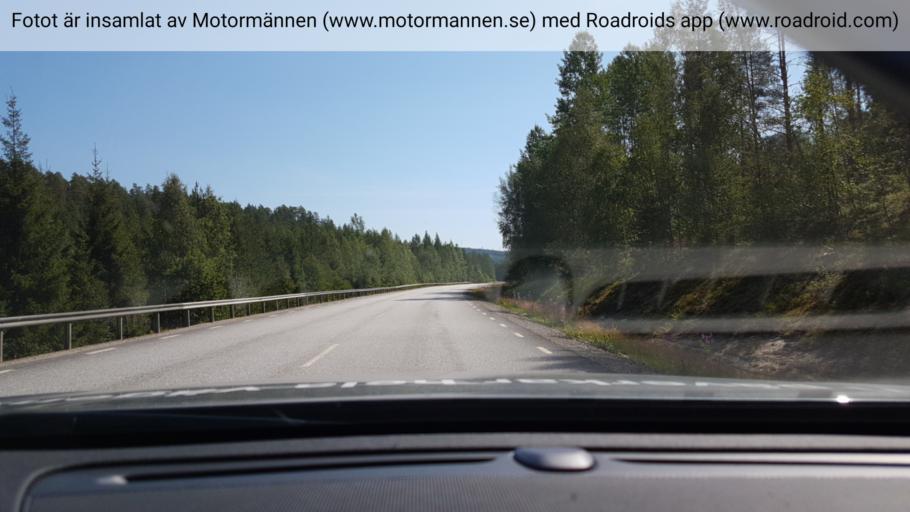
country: SE
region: Vaesterbotten
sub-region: Vindelns Kommun
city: Vindeln
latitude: 64.3158
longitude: 19.5826
